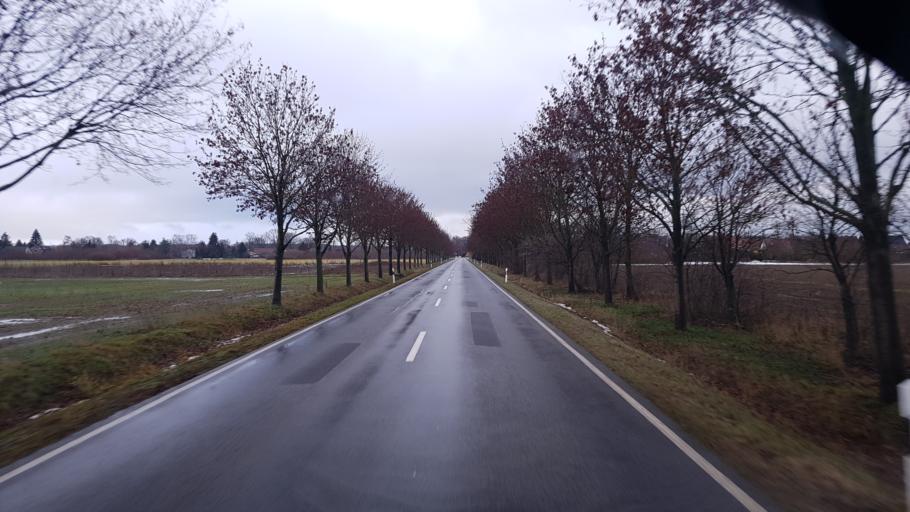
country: DE
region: Brandenburg
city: Schenkendobern
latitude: 51.8892
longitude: 14.6457
